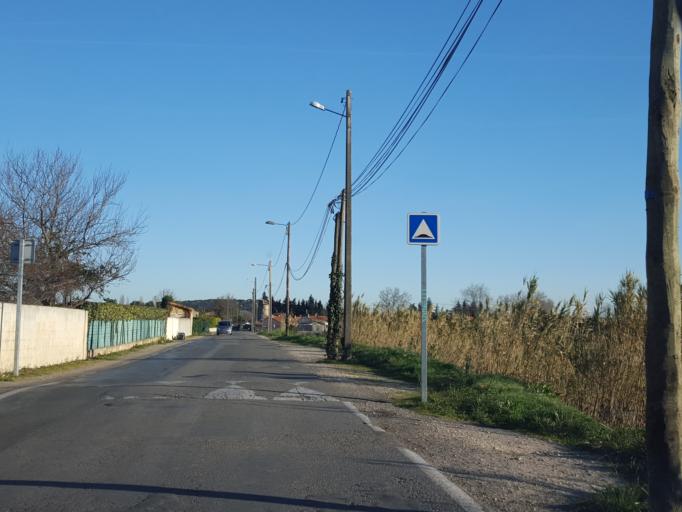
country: FR
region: Provence-Alpes-Cote d'Azur
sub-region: Departement du Vaucluse
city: Sorgues
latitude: 43.9903
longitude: 4.8718
